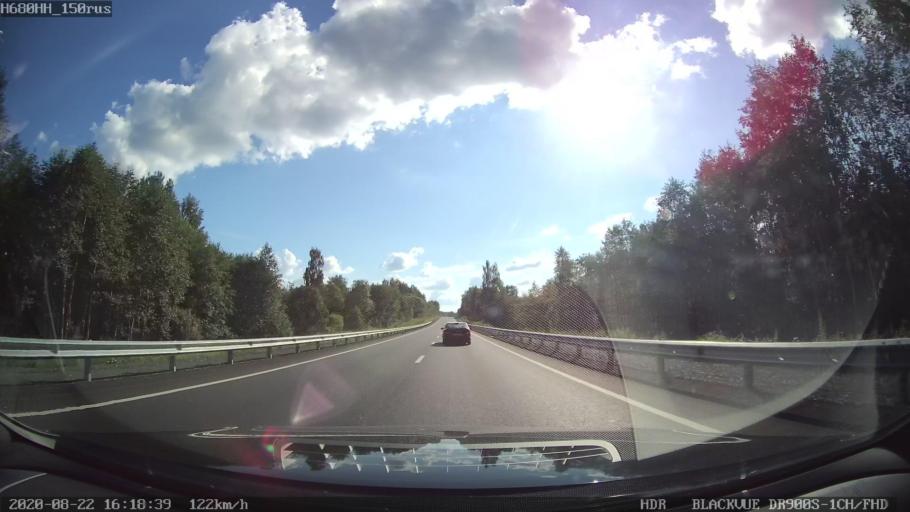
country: RU
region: Tverskaya
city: Rameshki
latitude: 57.4137
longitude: 36.1358
